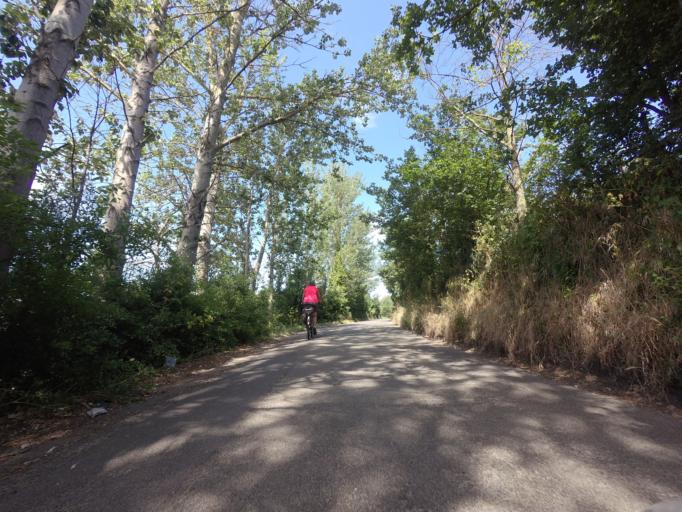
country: GB
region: England
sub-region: Kent
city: Strood
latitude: 51.4179
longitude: 0.4991
